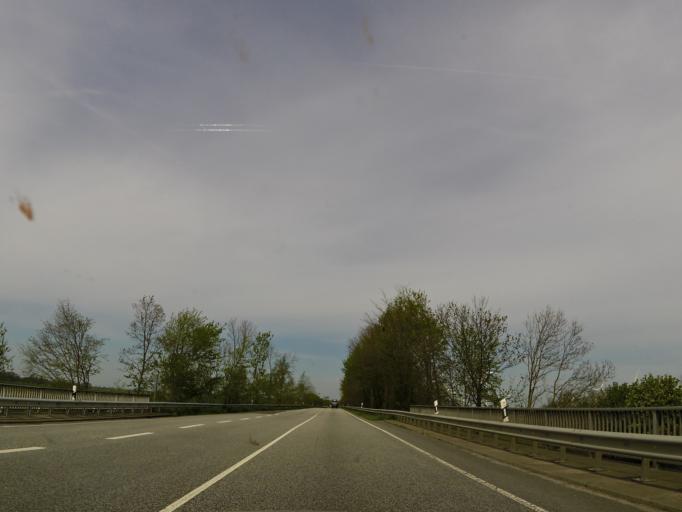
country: DE
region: Schleswig-Holstein
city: Hemme
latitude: 54.2765
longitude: 9.0074
